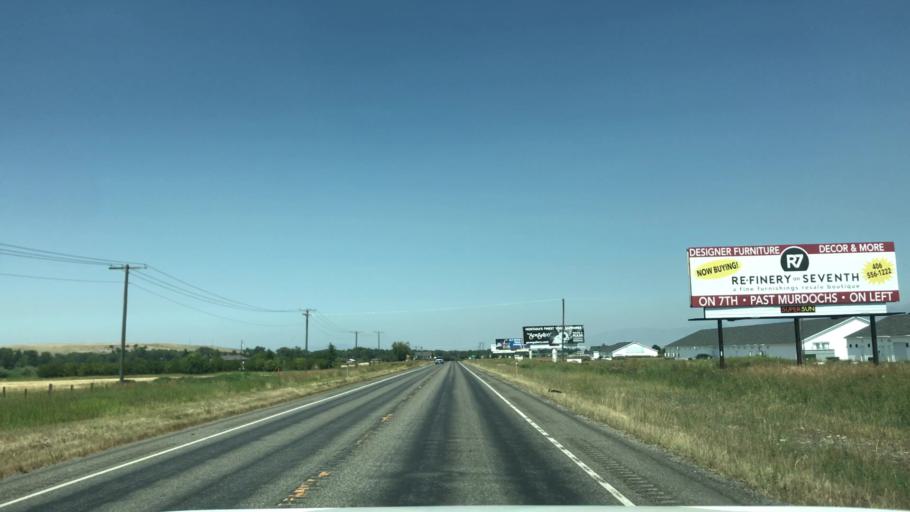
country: US
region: Montana
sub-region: Gallatin County
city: Four Corners
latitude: 45.6332
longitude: -111.1968
